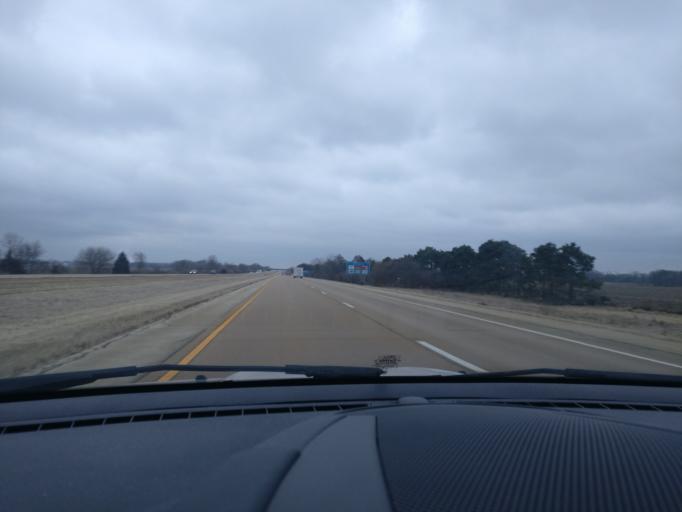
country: US
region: Illinois
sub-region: Whiteside County
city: Rock Falls
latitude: 41.7512
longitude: -89.7260
